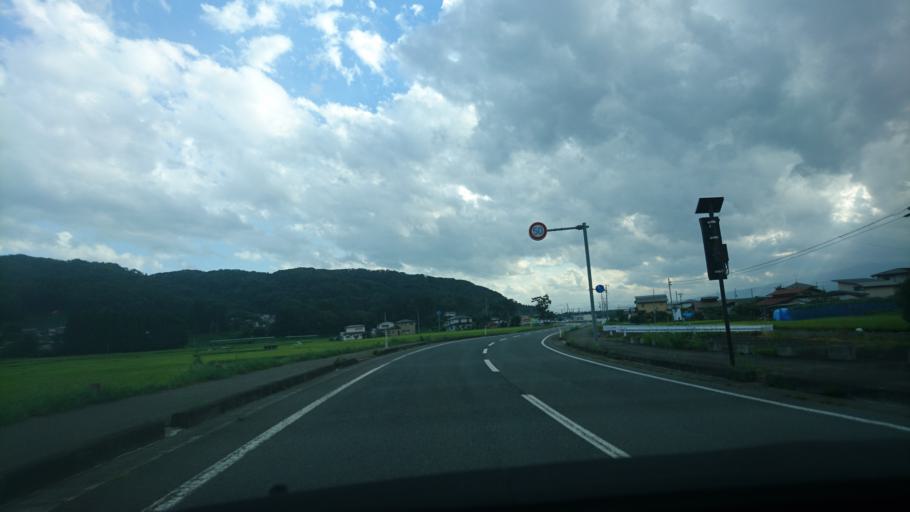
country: JP
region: Iwate
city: Kitakami
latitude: 39.2825
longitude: 141.1370
